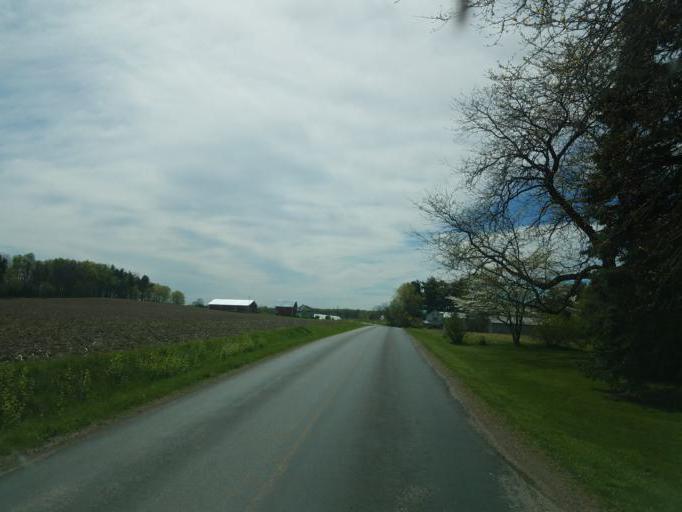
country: US
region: Ohio
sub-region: Richland County
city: Shelby
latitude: 40.9020
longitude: -82.5863
